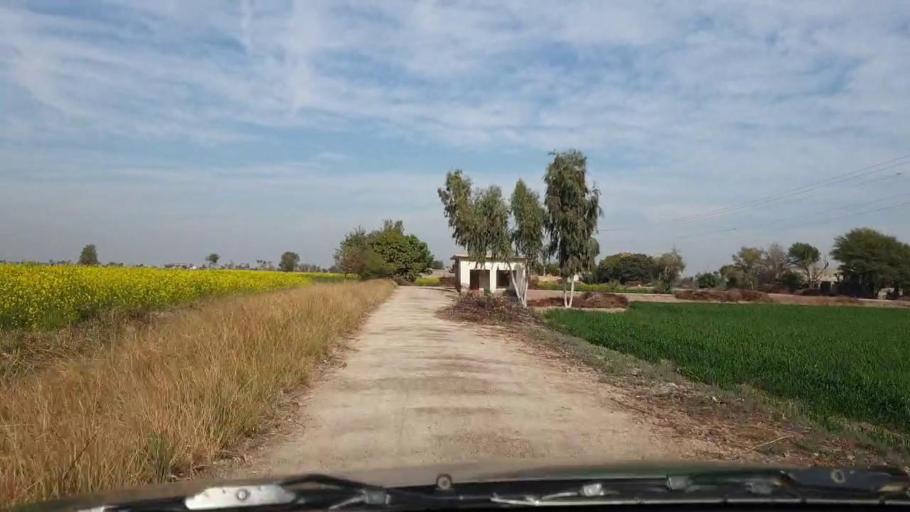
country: PK
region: Sindh
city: Jam Sahib
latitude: 26.2497
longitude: 68.6965
